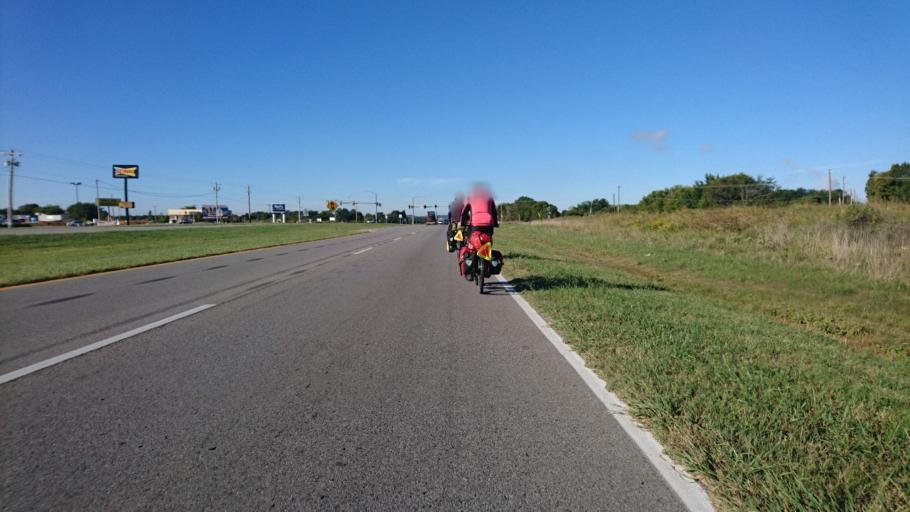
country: US
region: Oklahoma
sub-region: Rogers County
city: Verdigris
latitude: 36.2351
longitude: -95.6888
